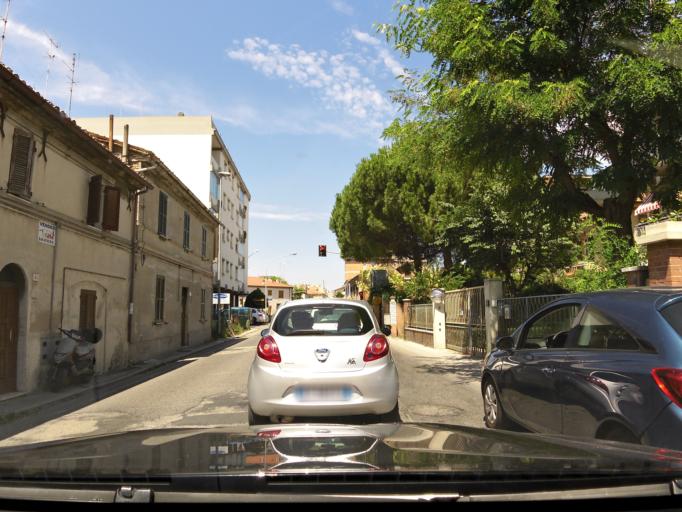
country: IT
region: The Marches
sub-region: Provincia di Ancona
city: Senigallia
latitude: 43.7194
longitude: 13.2161
